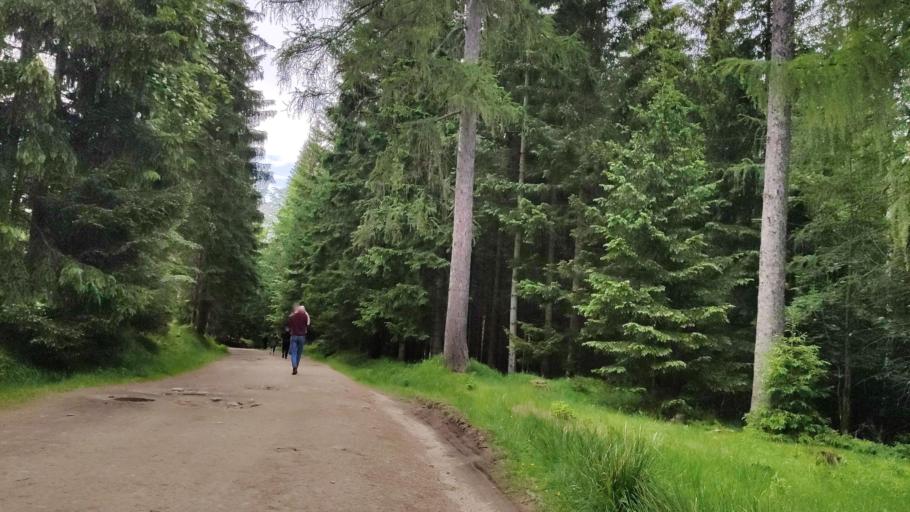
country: PL
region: Lower Silesian Voivodeship
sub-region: Powiat jeleniogorski
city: Szklarska Poreba
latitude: 50.8196
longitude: 15.5017
